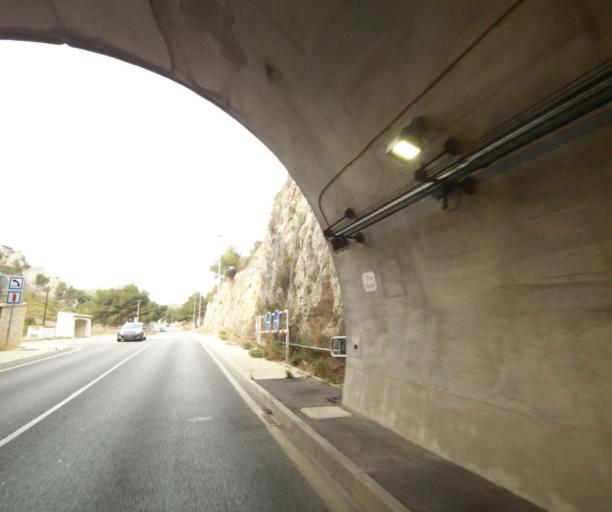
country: FR
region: Provence-Alpes-Cote d'Azur
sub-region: Departement des Bouches-du-Rhone
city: Le Rove
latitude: 43.3567
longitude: 5.2783
